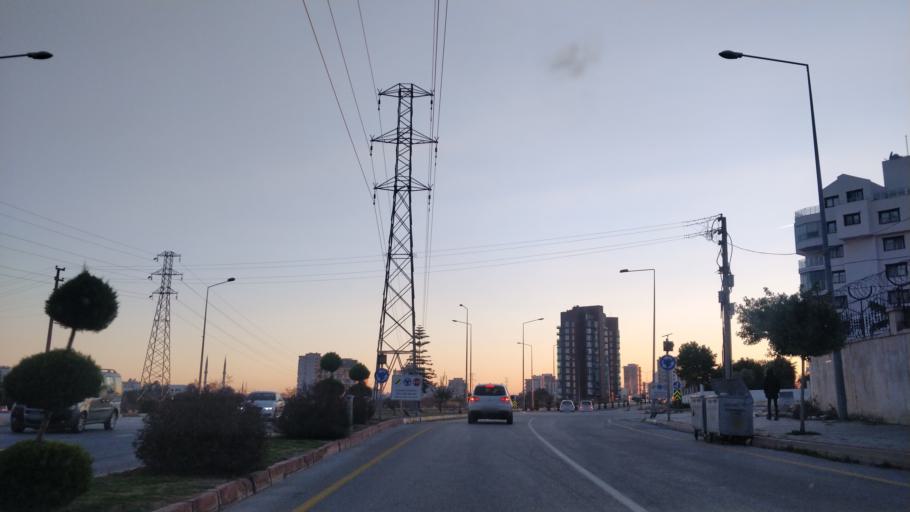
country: TR
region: Mersin
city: Mercin
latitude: 36.8035
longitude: 34.5706
